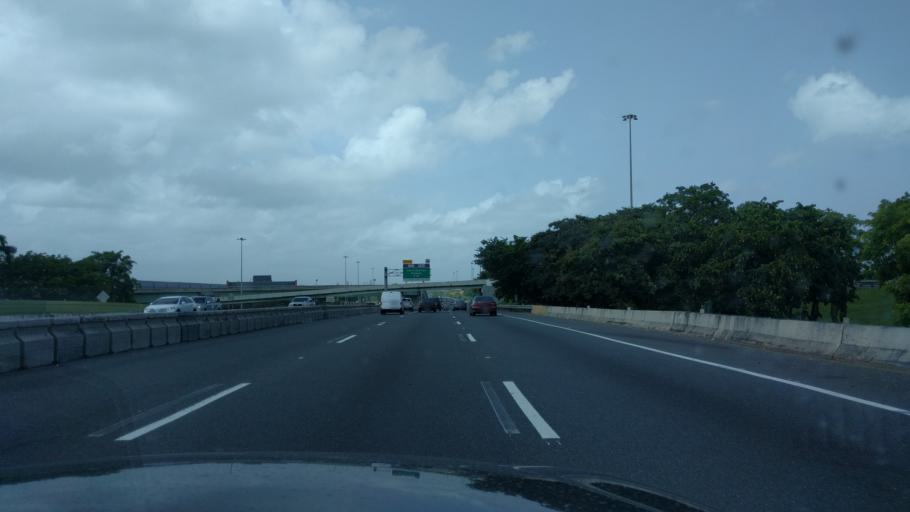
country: PR
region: Bayamon
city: Bayamon
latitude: 18.4228
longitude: -66.1405
